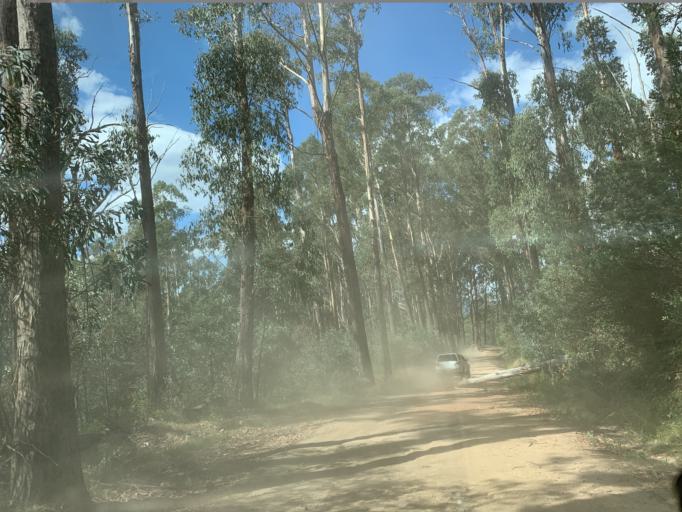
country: AU
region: Victoria
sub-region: Mansfield
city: Mansfield
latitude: -37.0970
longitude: 146.5335
